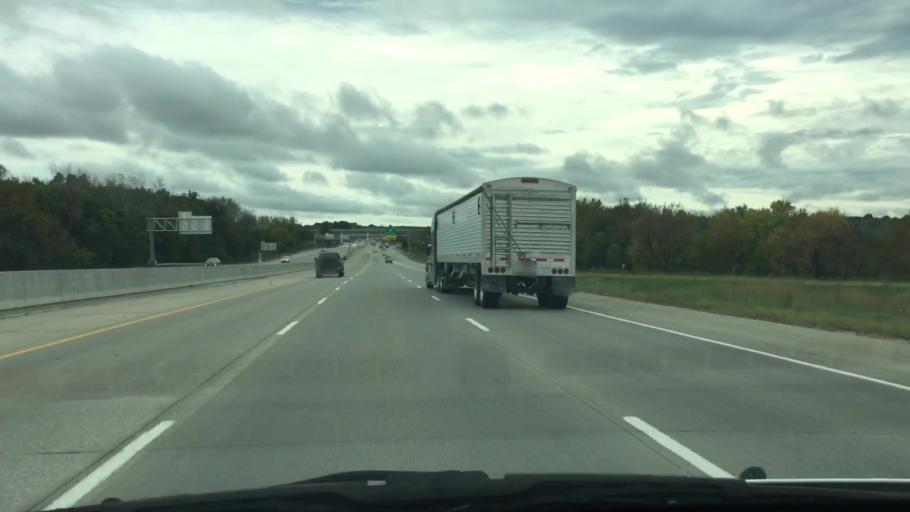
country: US
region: Iowa
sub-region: Polk County
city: West Des Moines
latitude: 41.5376
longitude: -93.7749
